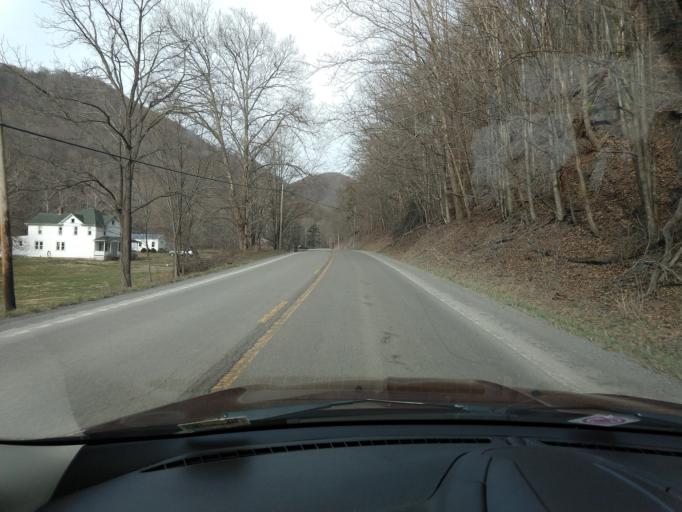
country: US
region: West Virginia
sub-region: Pendleton County
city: Franklin
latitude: 38.8623
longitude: -79.4461
